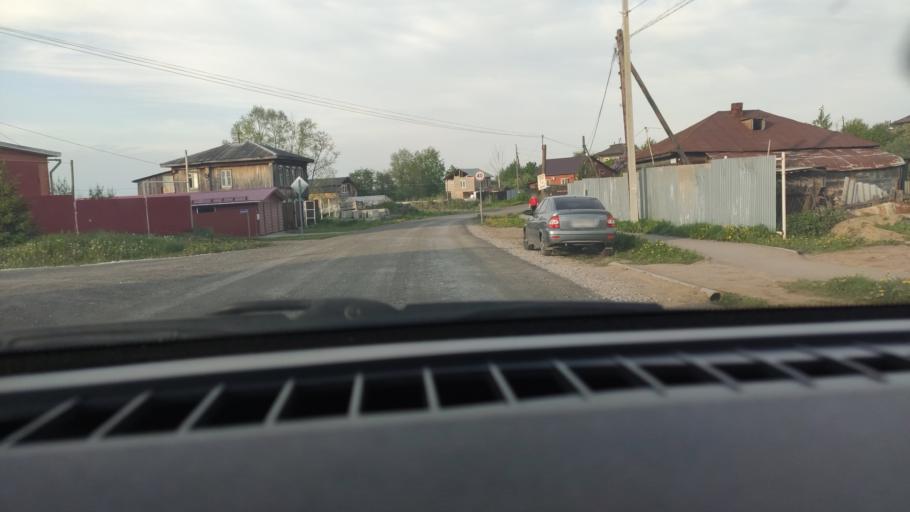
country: RU
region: Perm
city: Kondratovo
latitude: 57.9378
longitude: 56.0295
